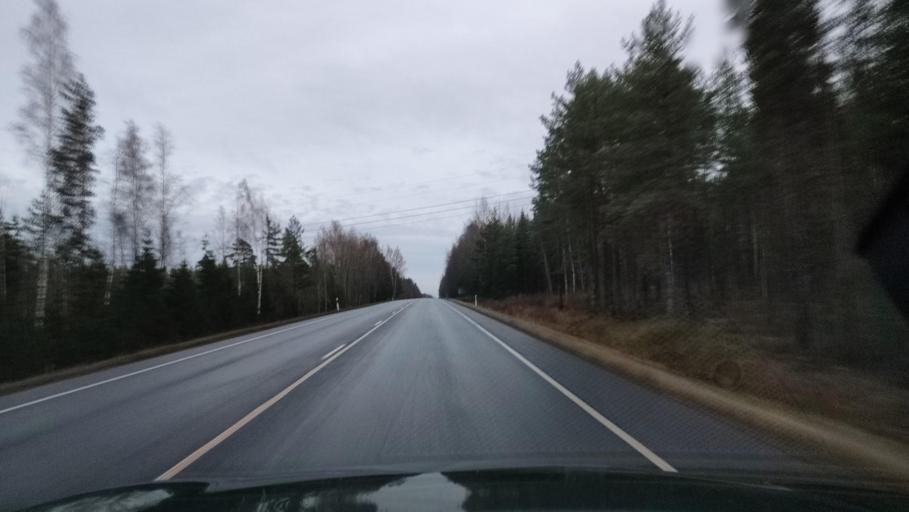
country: FI
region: Ostrobothnia
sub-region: Vaasa
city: Ristinummi
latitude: 63.0179
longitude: 21.7589
